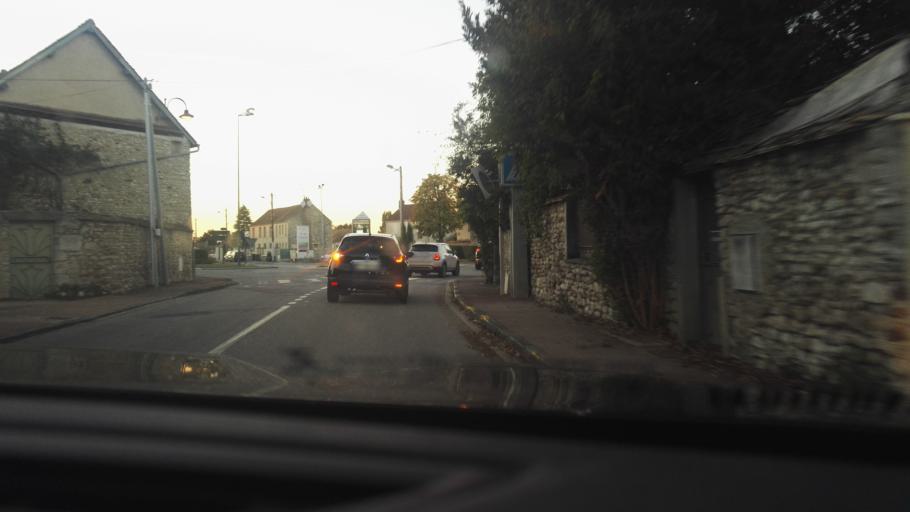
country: FR
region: Ile-de-France
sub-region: Departement des Yvelines
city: Longnes
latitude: 48.9203
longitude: 1.5847
